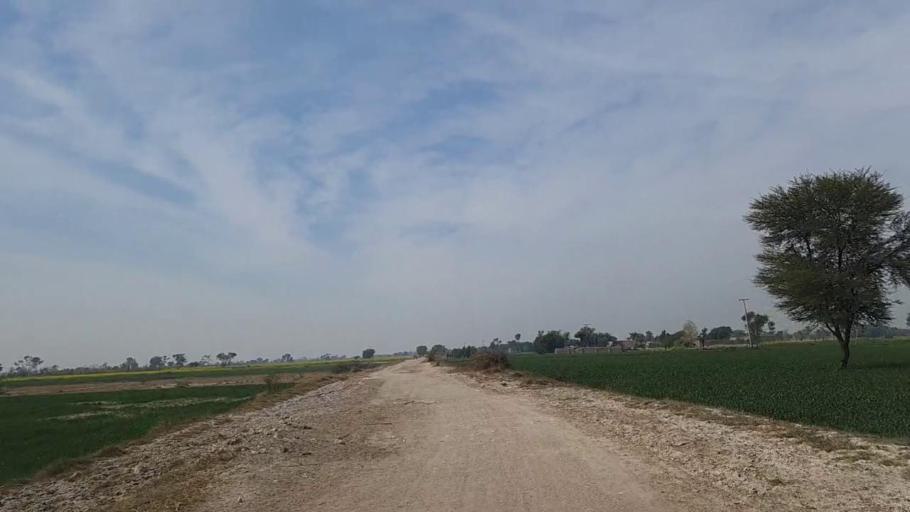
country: PK
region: Sindh
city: Nawabshah
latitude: 26.3276
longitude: 68.4338
